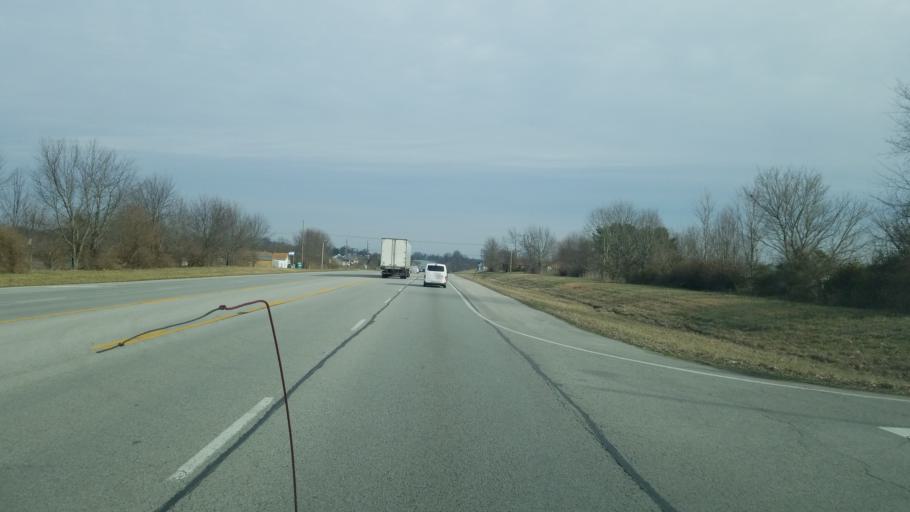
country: US
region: Kentucky
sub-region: Boyle County
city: Junction City
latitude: 37.5875
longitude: -84.7828
